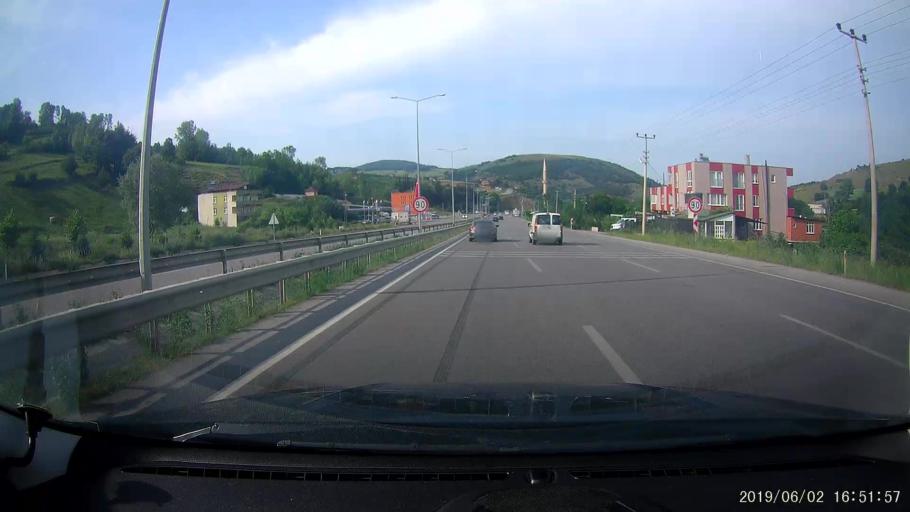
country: TR
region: Samsun
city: Samsun
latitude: 41.2808
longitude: 36.1906
